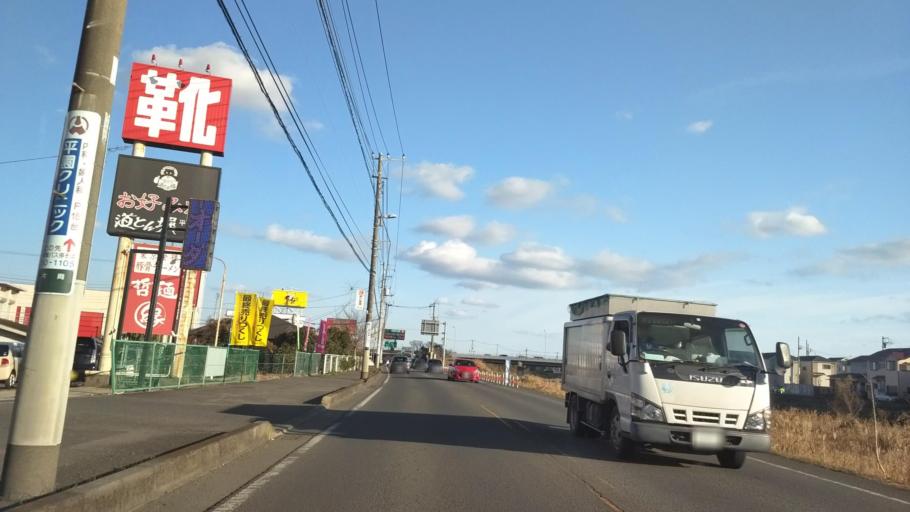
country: JP
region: Kanagawa
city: Isehara
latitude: 35.3592
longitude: 139.2998
